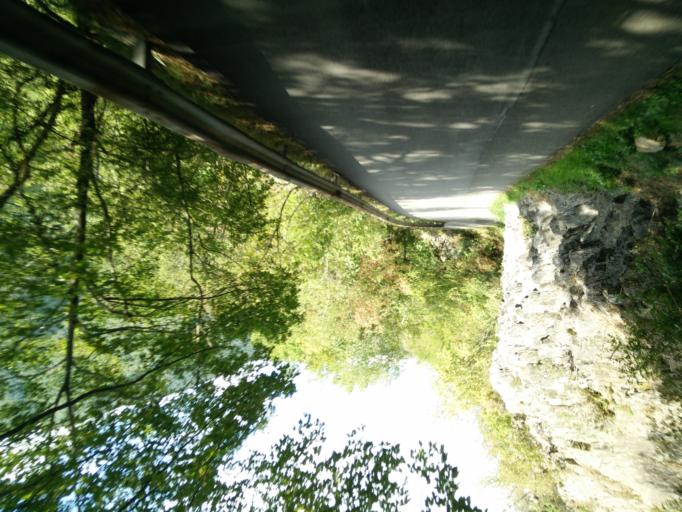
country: IT
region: Tuscany
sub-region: Provincia di Massa-Carrara
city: Zeri
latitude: 44.3522
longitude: 9.7913
